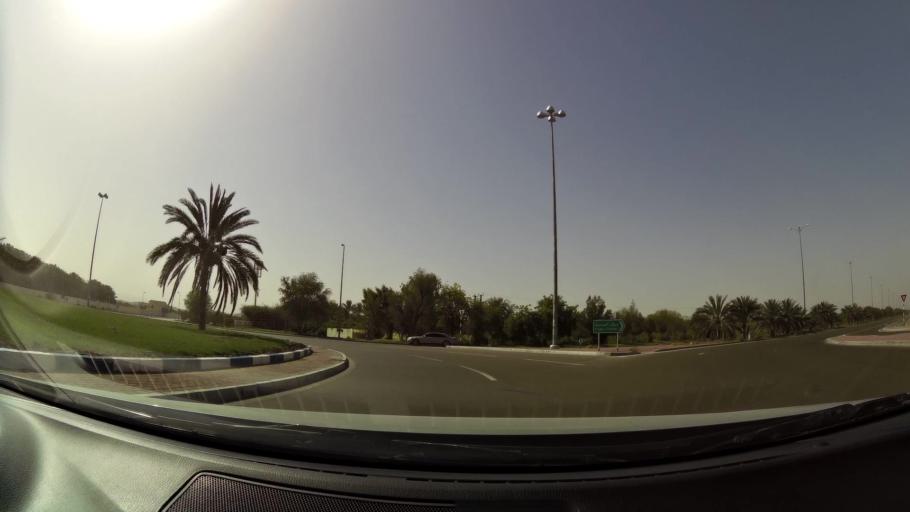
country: OM
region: Al Buraimi
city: Al Buraymi
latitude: 24.3152
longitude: 55.7966
